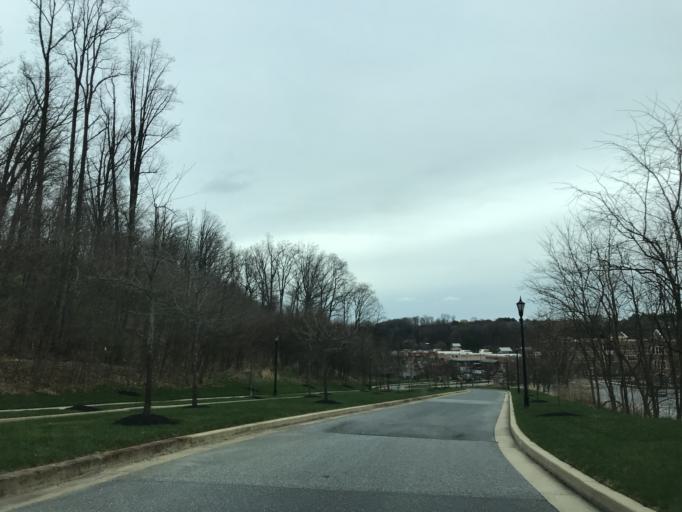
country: US
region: Maryland
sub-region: Baltimore County
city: Pikesville
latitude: 39.3856
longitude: -76.6935
